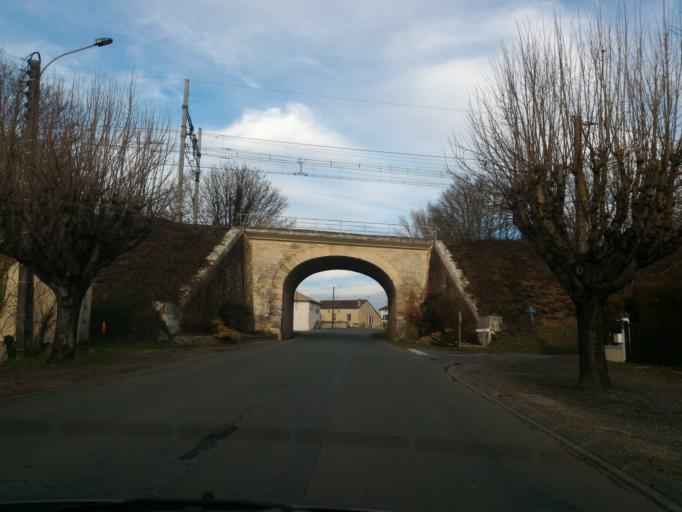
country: FR
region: Poitou-Charentes
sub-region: Departement de la Charente
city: Ruffec
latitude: 46.0328
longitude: 0.1967
